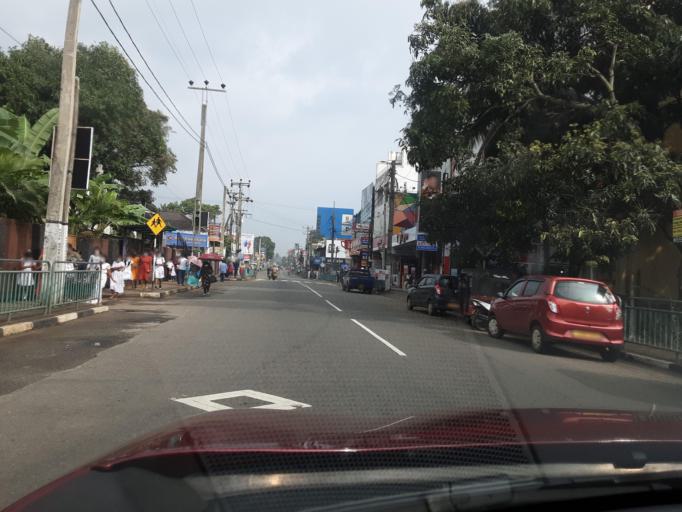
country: LK
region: Central
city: Kandy
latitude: 7.4702
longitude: 80.6227
